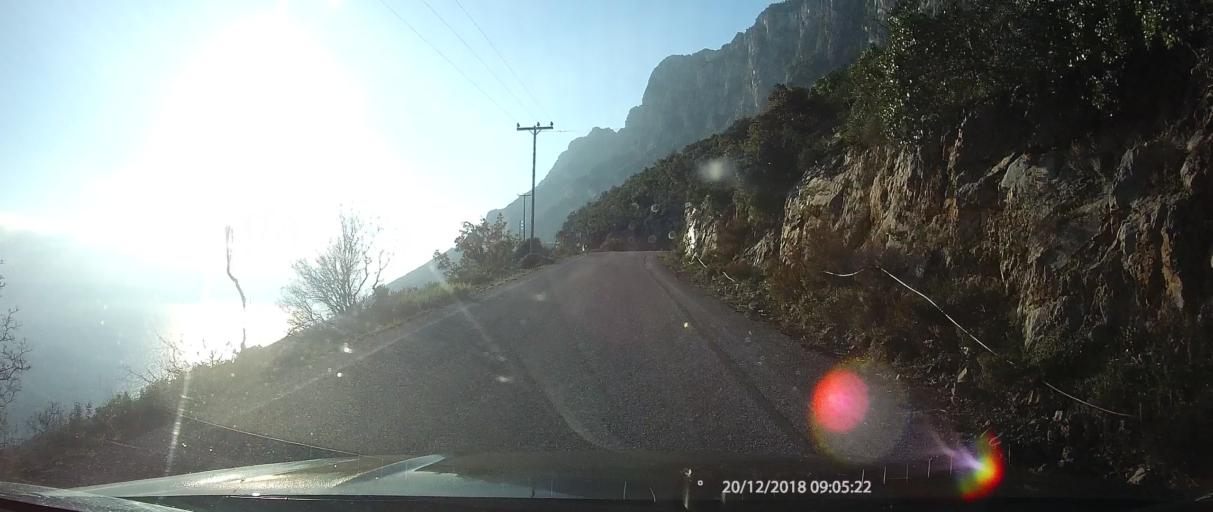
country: GR
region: Peloponnese
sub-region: Nomos Lakonias
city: Sykea
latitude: 36.9415
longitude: 22.9965
